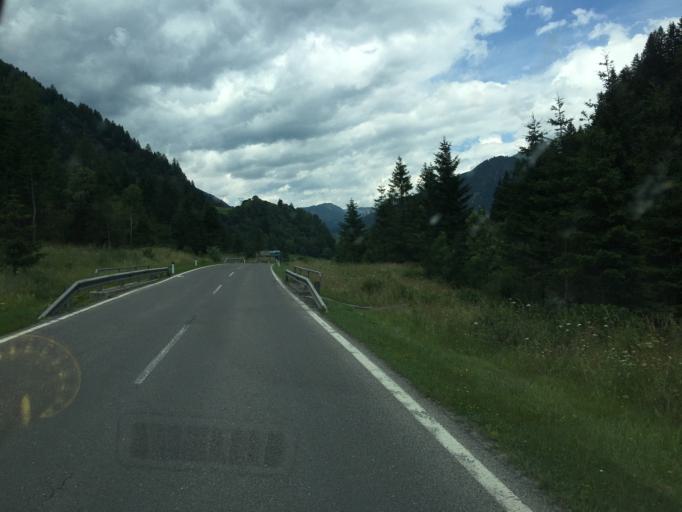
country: AT
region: Carinthia
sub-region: Politischer Bezirk Spittal an der Drau
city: Mortschach
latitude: 46.9391
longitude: 12.9007
